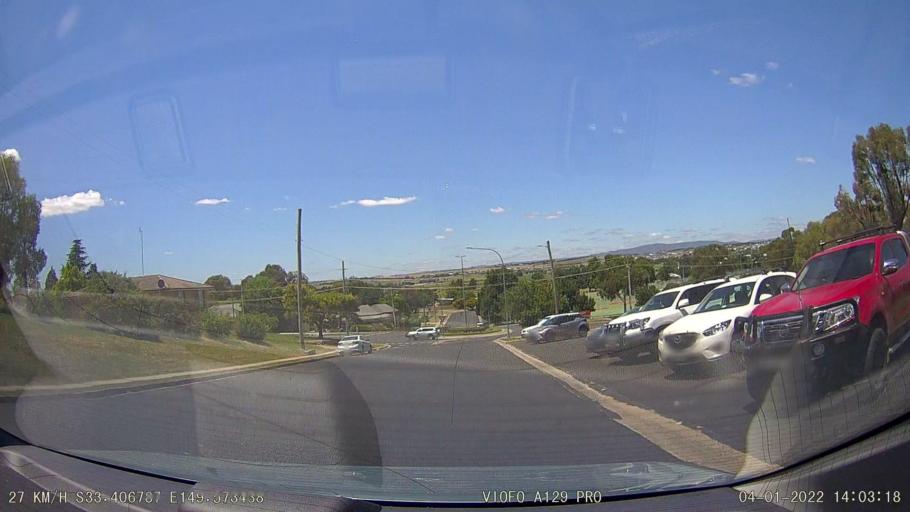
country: AU
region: New South Wales
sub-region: Bathurst Regional
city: Bathurst
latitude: -33.4068
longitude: 149.5734
